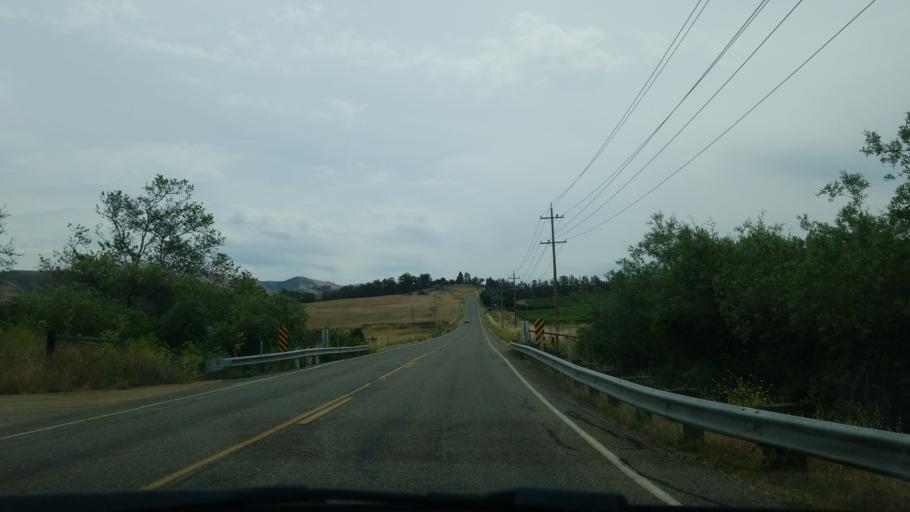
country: US
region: California
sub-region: San Luis Obispo County
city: San Luis Obispo
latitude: 35.2428
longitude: -120.6118
